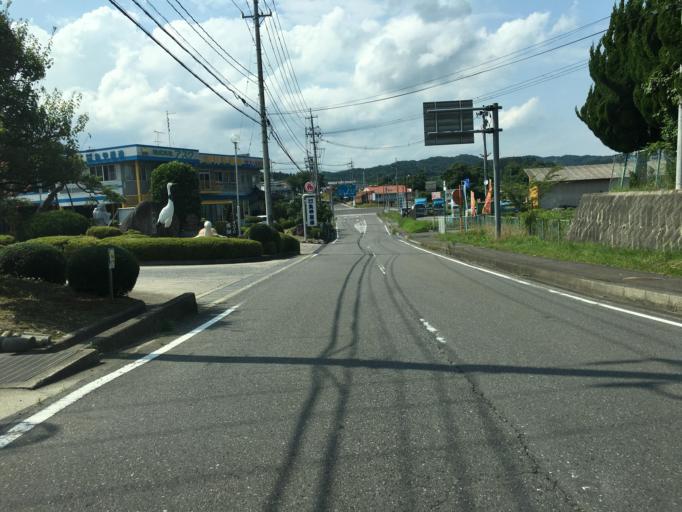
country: JP
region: Fukushima
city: Nihommatsu
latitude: 37.5787
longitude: 140.4240
